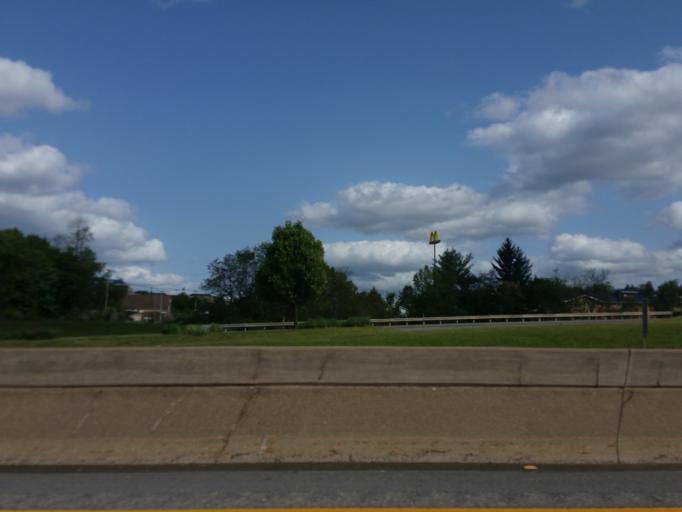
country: US
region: West Virginia
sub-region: Raleigh County
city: Mabscott
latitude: 37.7938
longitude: -81.2159
